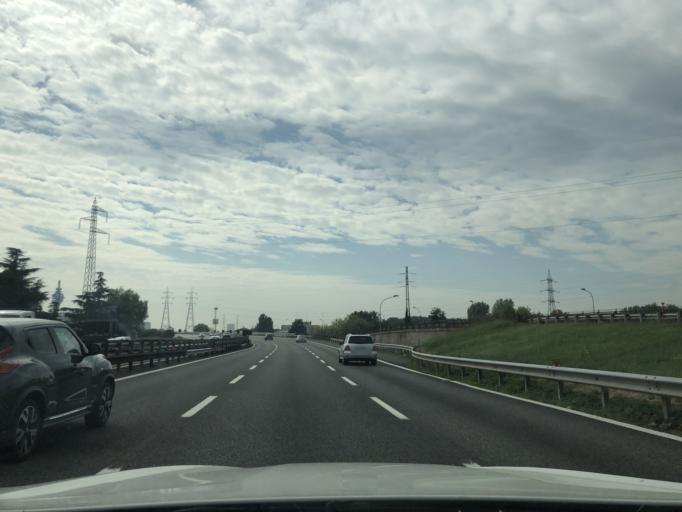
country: IT
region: Lombardy
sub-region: Citta metropolitana di Milano
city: Cologno Monzese
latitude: 45.5309
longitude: 9.2696
